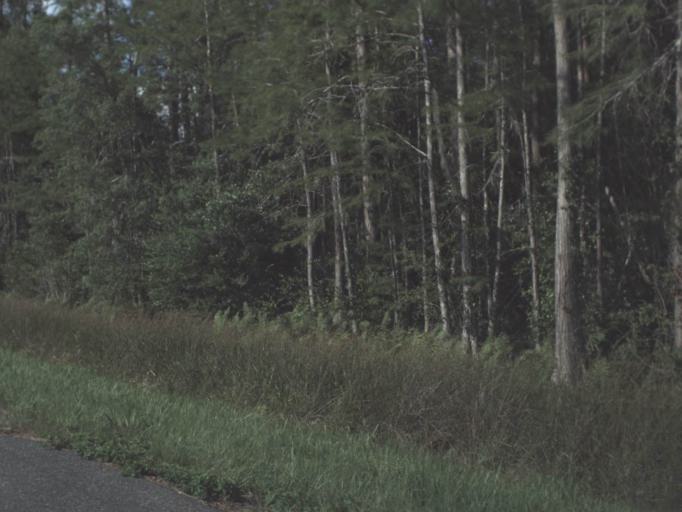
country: US
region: Florida
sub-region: Lafayette County
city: Mayo
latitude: 30.0132
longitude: -83.1934
